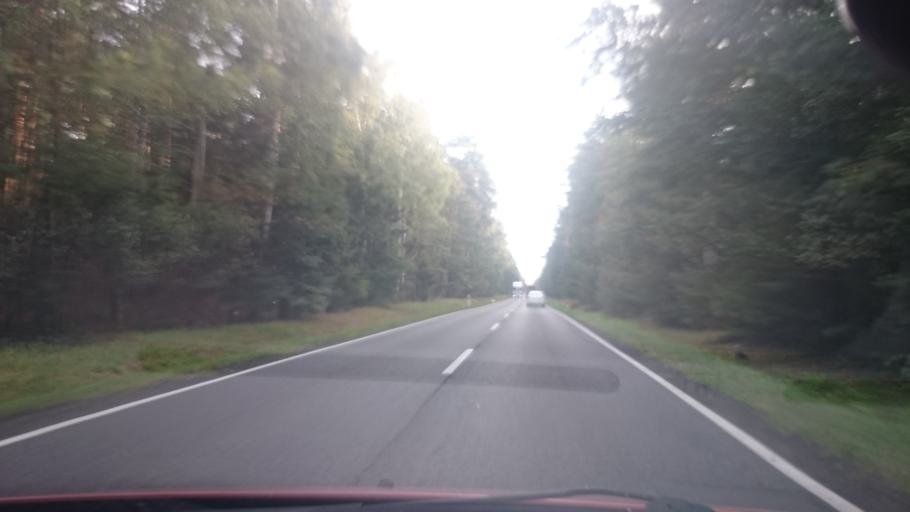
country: PL
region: Lower Silesian Voivodeship
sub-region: Powiat milicki
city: Sulow
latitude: 51.4105
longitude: 17.2180
